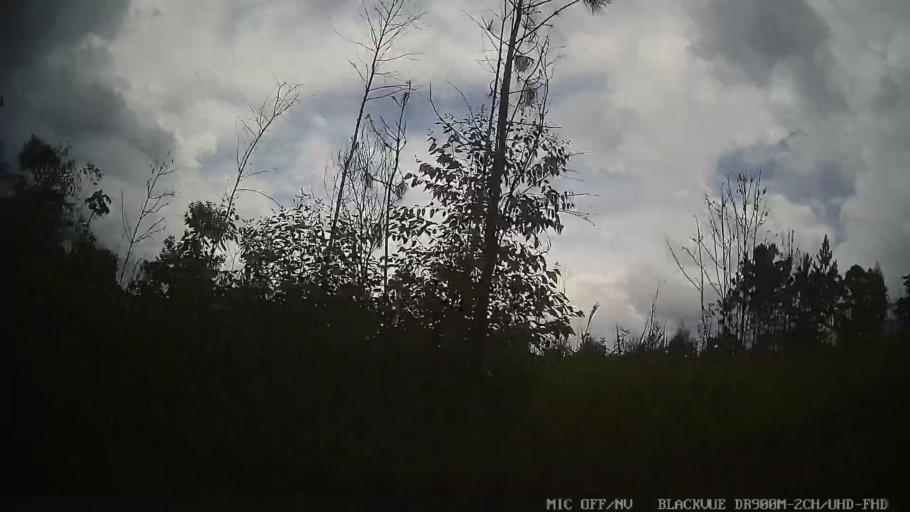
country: BR
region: Sao Paulo
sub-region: Mogi das Cruzes
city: Mogi das Cruzes
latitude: -23.4583
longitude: -46.2241
